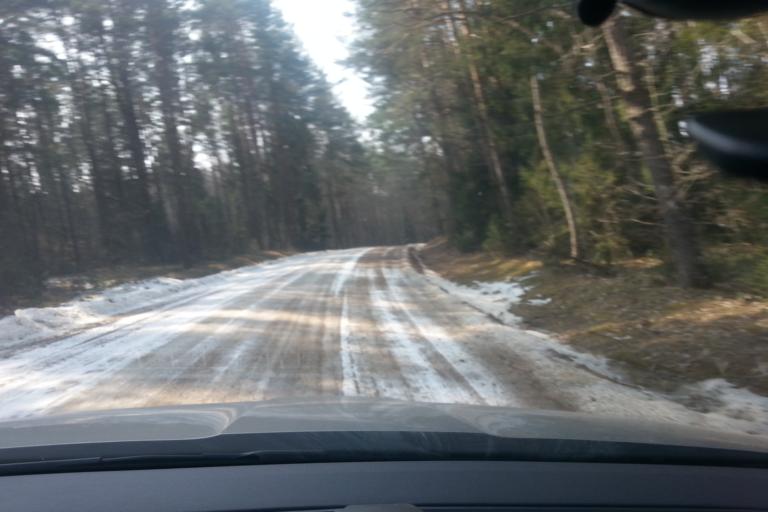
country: LT
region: Vilnius County
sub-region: Trakai
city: Rudiskes
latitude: 54.5121
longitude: 24.9347
